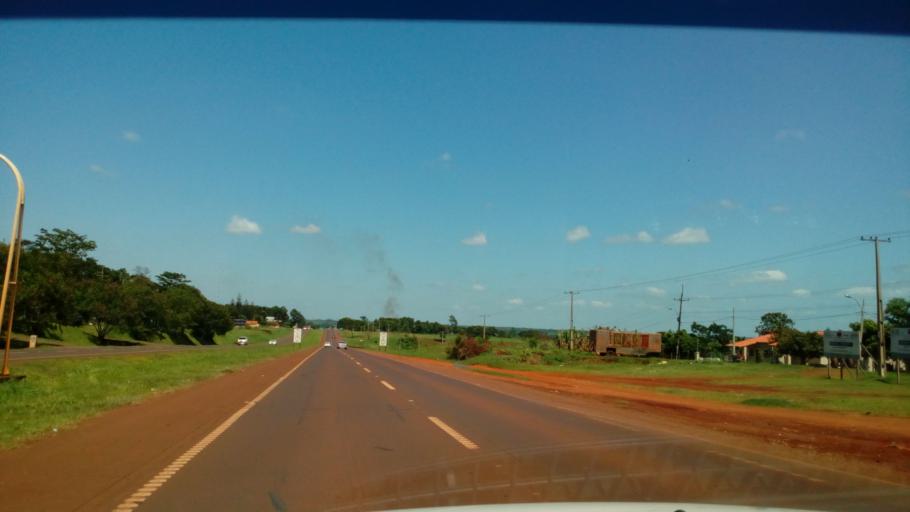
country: PY
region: Alto Parana
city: Colonia Yguazu
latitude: -25.4864
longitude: -54.8644
